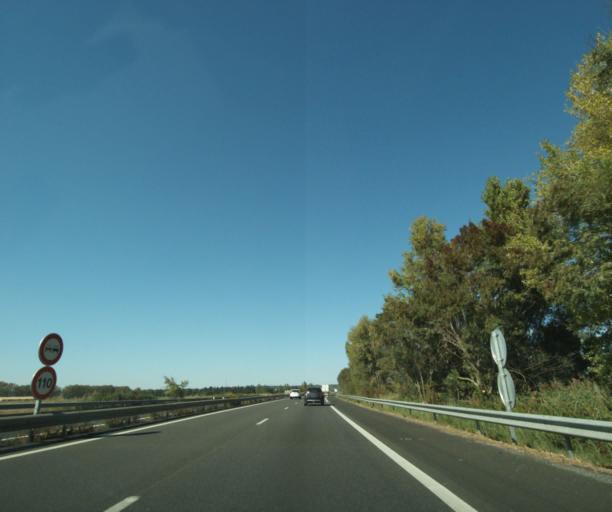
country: FR
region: Languedoc-Roussillon
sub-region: Departement du Gard
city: Bellegarde
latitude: 43.7153
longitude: 4.5122
